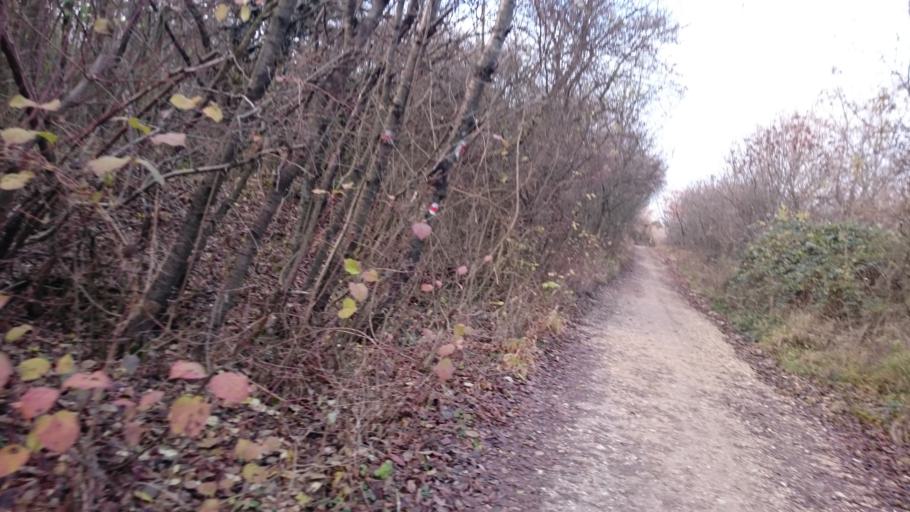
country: HU
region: Pest
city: Urom
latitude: 47.6092
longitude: 19.0121
